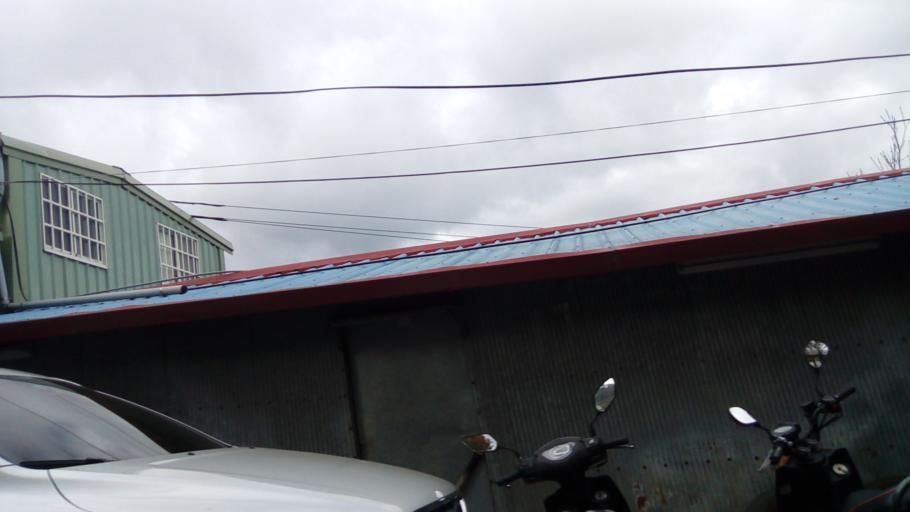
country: TW
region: Taiwan
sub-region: Nantou
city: Puli
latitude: 24.2583
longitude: 121.2557
